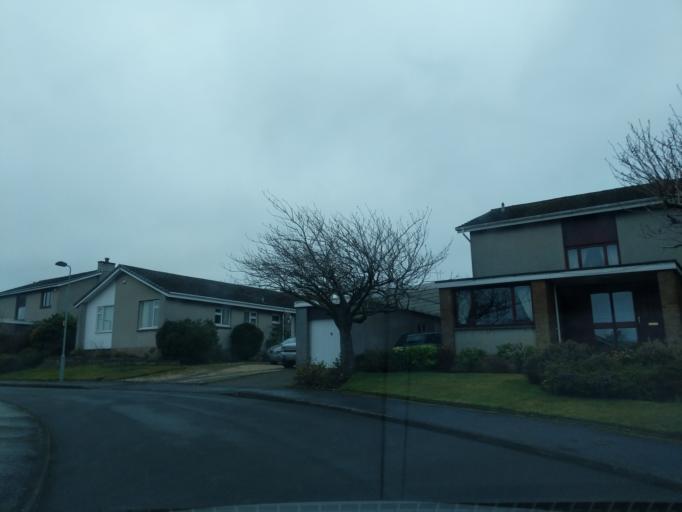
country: GB
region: Scotland
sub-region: Edinburgh
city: Balerno
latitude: 55.8908
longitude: -3.3308
